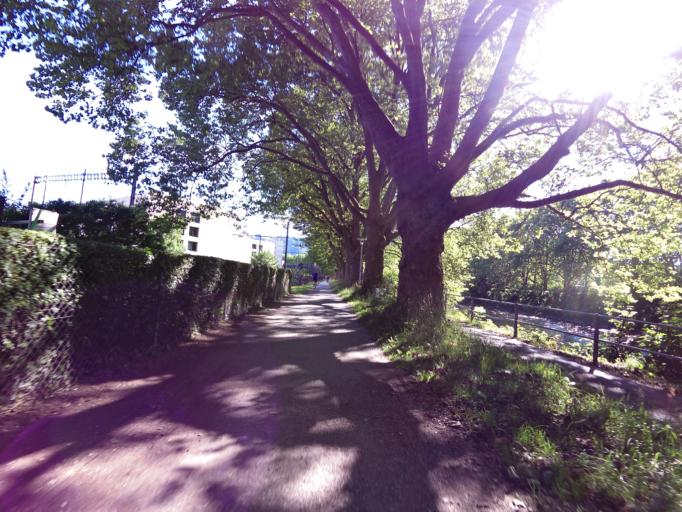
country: CH
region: Zurich
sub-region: Bezirk Zuerich
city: Zuerich (Kreis 4) / Werd
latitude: 47.3675
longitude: 8.5267
